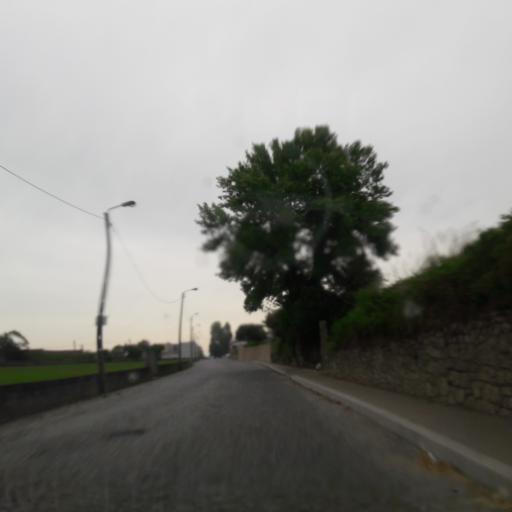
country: PT
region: Porto
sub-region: Vila do Conde
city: Arvore
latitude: 41.3390
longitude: -8.7340
